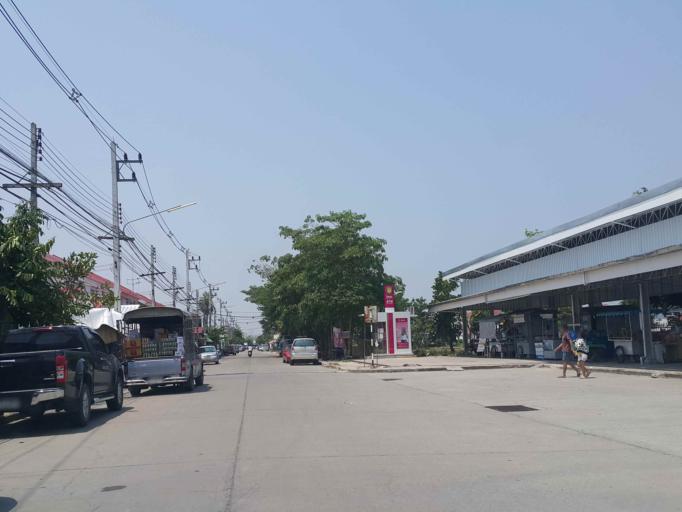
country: TH
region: Chiang Mai
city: San Kamphaeng
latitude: 18.7479
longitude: 99.0881
